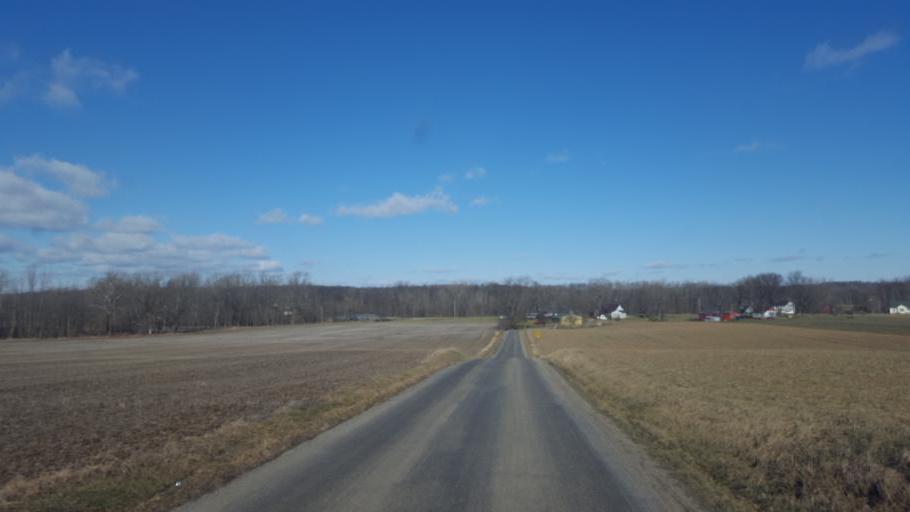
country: US
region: Ohio
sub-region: Richland County
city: Lexington
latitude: 40.6177
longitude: -82.6137
